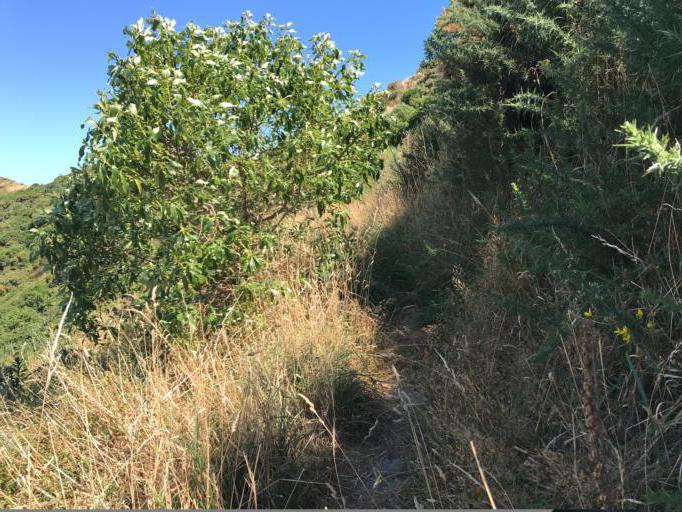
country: NZ
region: Wellington
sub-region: Wellington City
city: Brooklyn
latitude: -41.3308
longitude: 174.7665
